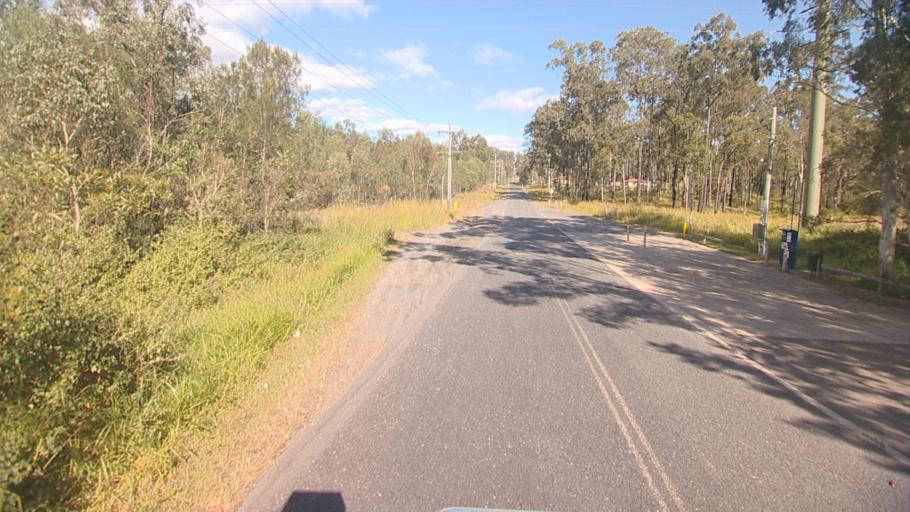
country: AU
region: Queensland
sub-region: Logan
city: Chambers Flat
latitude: -27.8035
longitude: 153.0831
